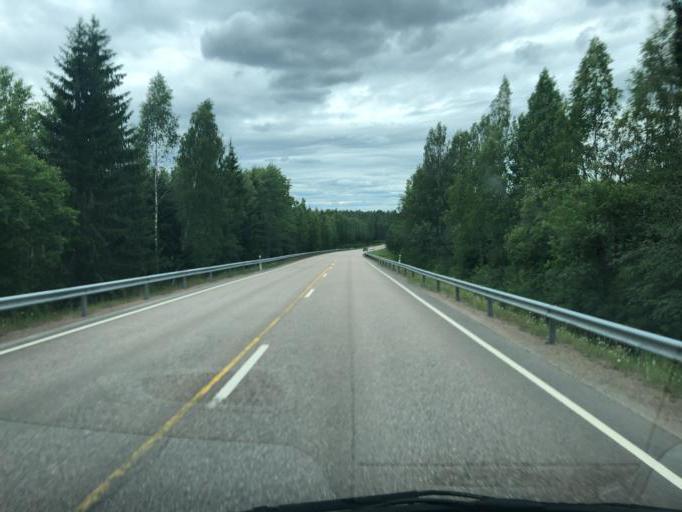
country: FI
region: Southern Savonia
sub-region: Mikkeli
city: Maentyharju
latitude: 61.1114
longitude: 27.1009
